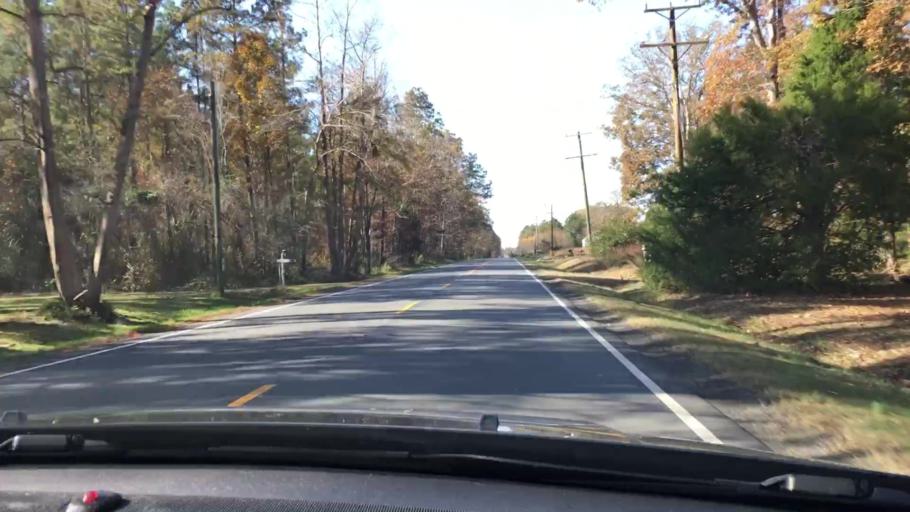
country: US
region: Virginia
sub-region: King William County
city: King William
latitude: 37.6896
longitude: -77.0213
